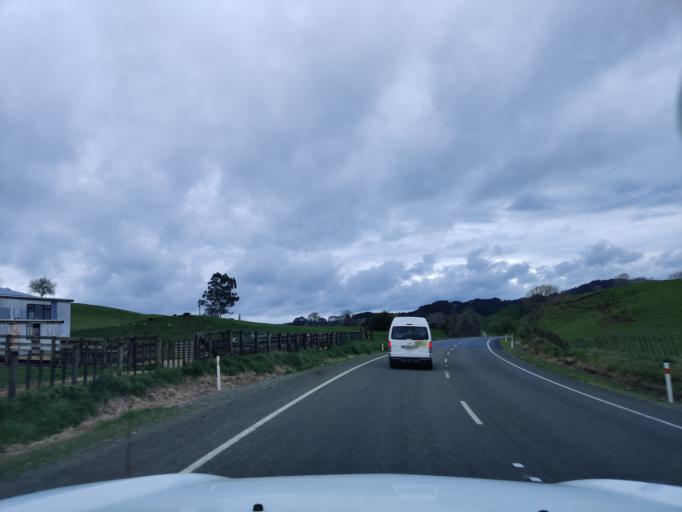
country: NZ
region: Waikato
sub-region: Otorohanga District
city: Otorohanga
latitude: -38.4543
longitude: 175.1645
